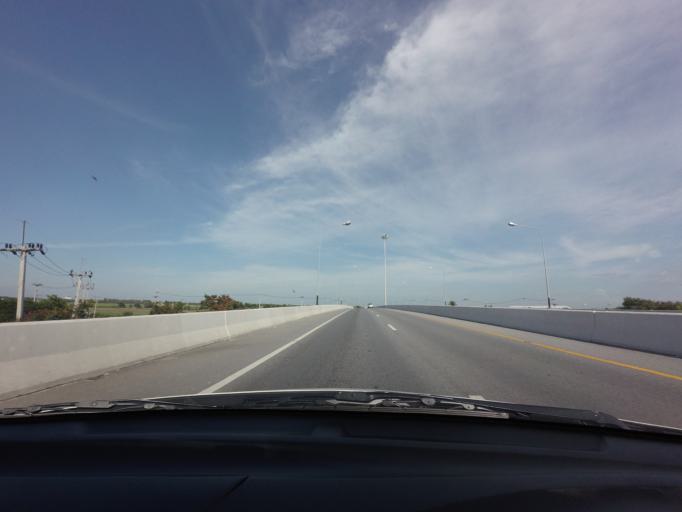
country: TH
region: Suphan Buri
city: Suphan Buri
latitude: 14.4649
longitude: 100.0466
